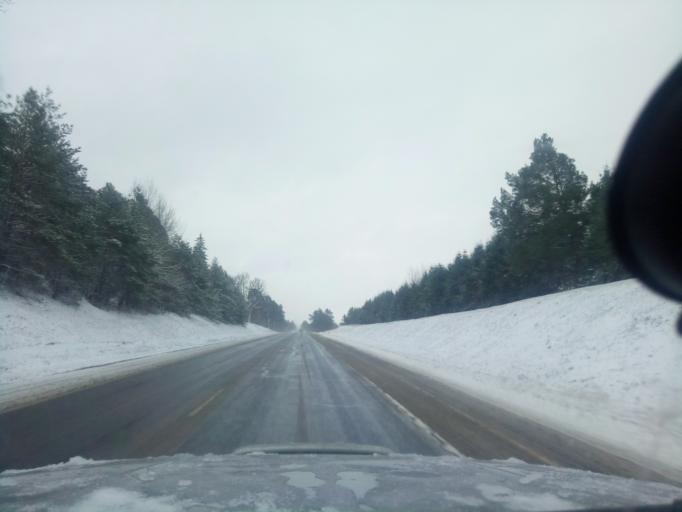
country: BY
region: Minsk
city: Nyasvizh
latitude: 53.2612
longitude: 26.6101
